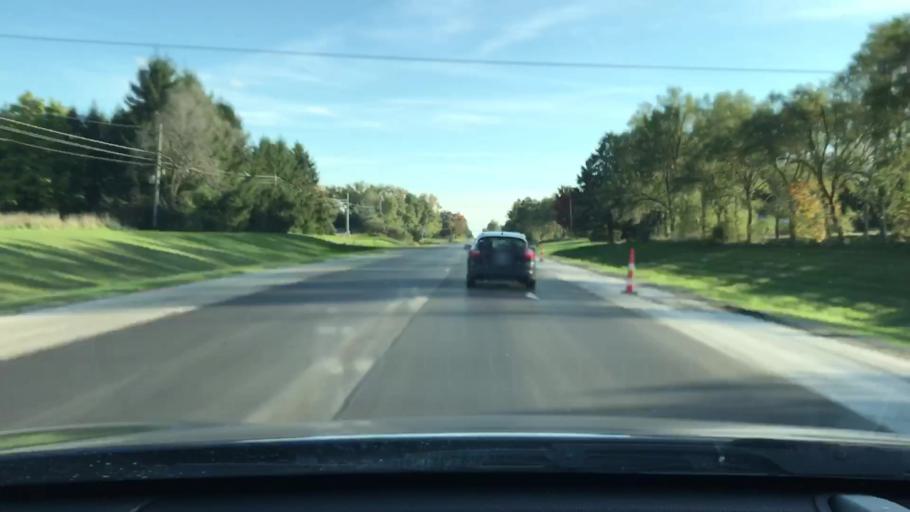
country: US
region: Michigan
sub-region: Shiawassee County
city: Owosso
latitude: 42.9399
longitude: -84.2227
